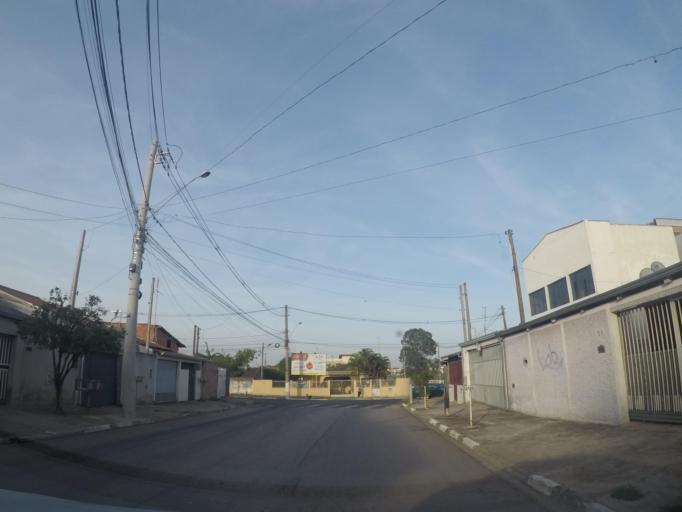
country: BR
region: Sao Paulo
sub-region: Hortolandia
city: Hortolandia
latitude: -22.8486
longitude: -47.1798
